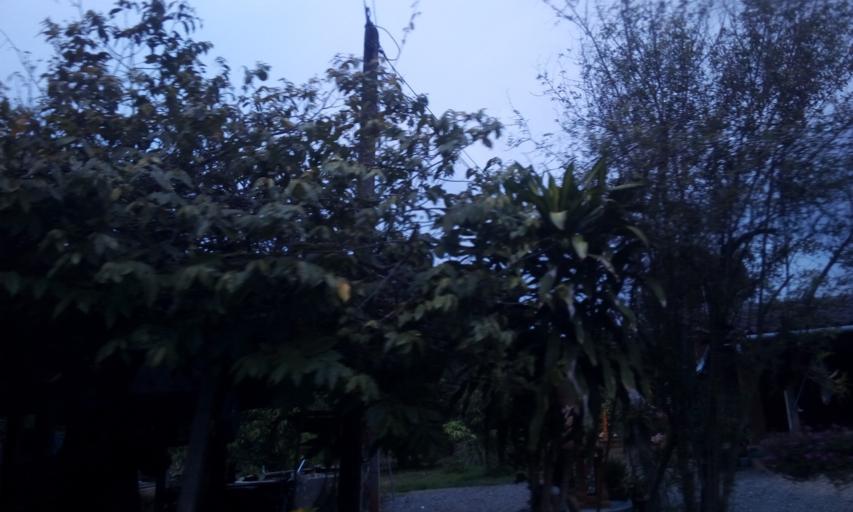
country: TH
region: Trat
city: Laem Ngop
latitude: 12.2149
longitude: 102.3025
